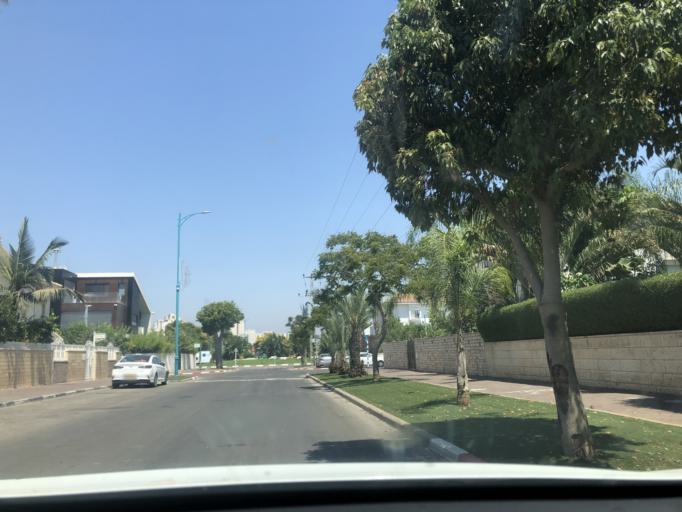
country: IL
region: Central District
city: Lod
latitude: 31.9419
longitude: 34.8934
